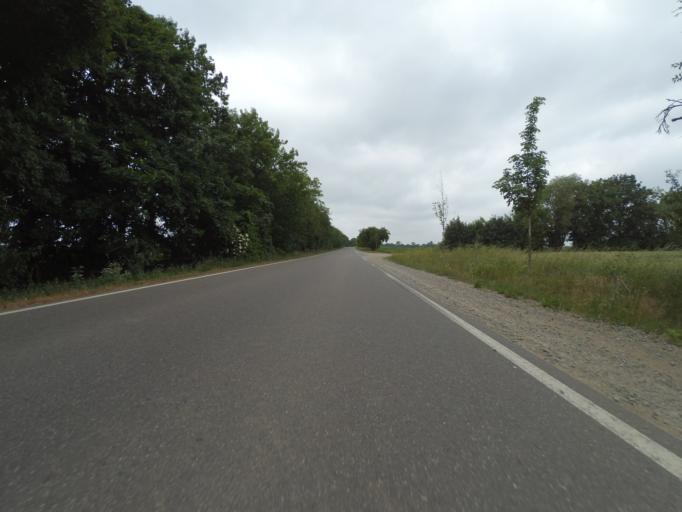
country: DE
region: Mecklenburg-Vorpommern
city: Krakow am See
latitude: 53.6340
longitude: 12.3595
